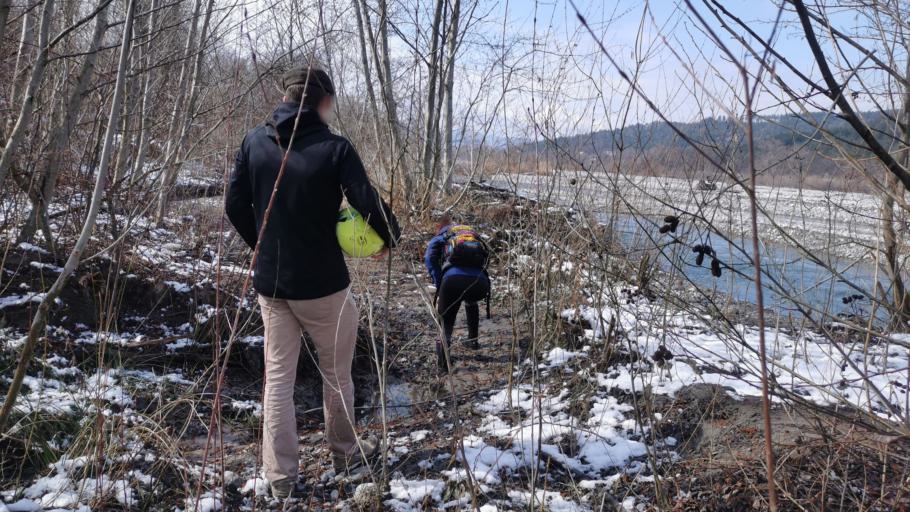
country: FR
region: Provence-Alpes-Cote d'Azur
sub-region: Departement des Alpes-de-Haute-Provence
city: Mallemoisson
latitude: 44.0613
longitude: 6.1707
